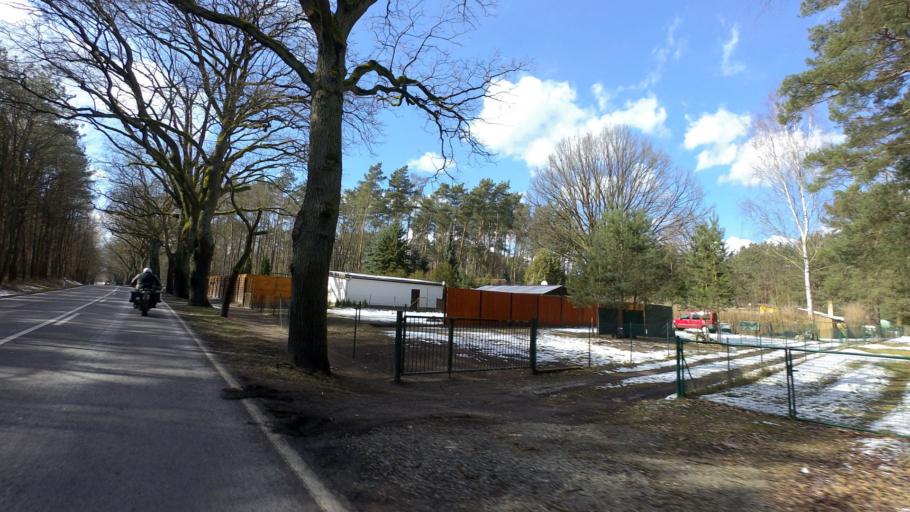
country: DE
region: Brandenburg
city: Marienwerder
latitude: 52.8557
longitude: 13.6414
